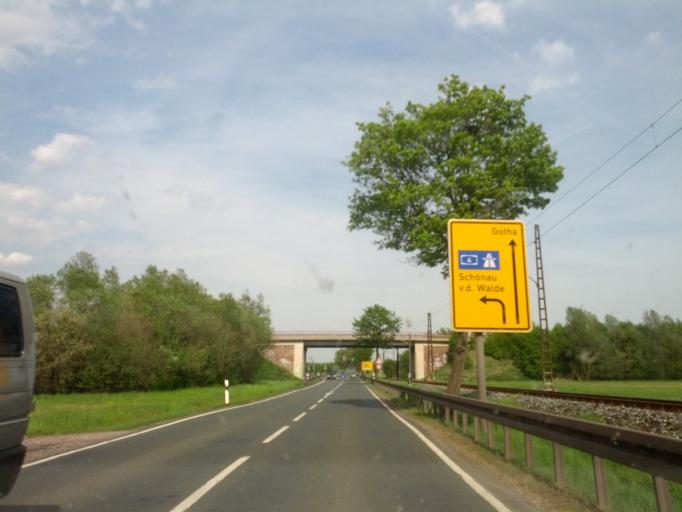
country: DE
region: Thuringia
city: Horselgau
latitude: 50.9029
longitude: 10.6101
